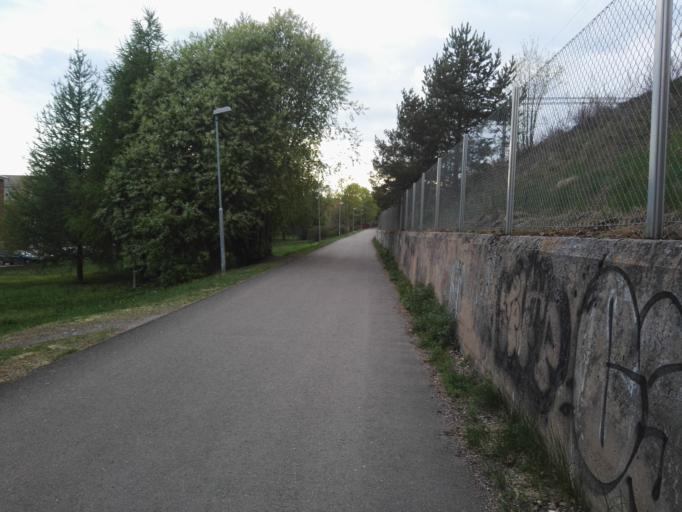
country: FI
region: Paijanne Tavastia
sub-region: Lahti
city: Lahti
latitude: 60.9763
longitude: 25.6514
